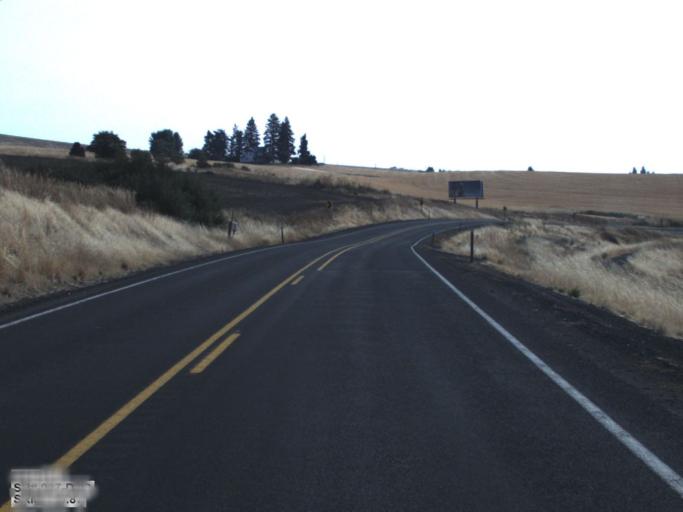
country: US
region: Idaho
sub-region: Benewah County
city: Plummer
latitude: 47.2321
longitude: -117.0982
